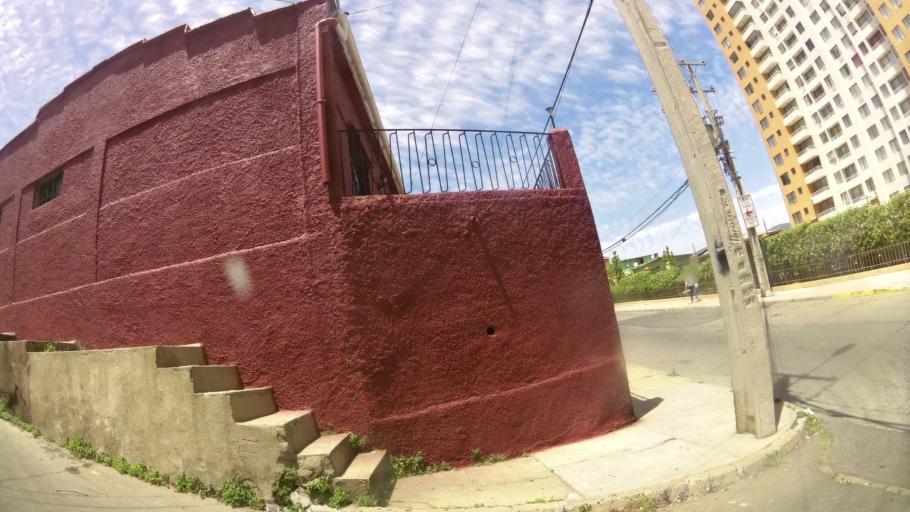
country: CL
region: Valparaiso
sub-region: Provincia de Valparaiso
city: Valparaiso
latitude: -33.0460
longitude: -71.5967
